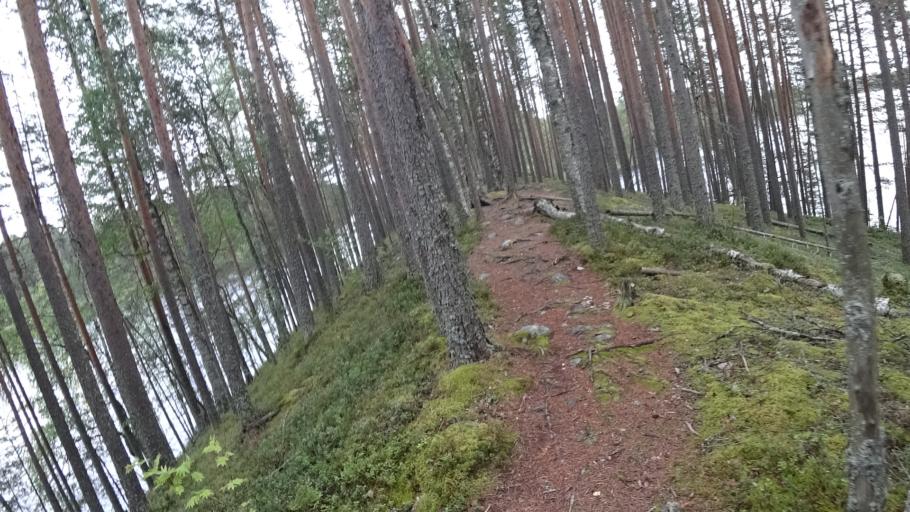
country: FI
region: North Karelia
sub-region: Joensuu
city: Ilomantsi
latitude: 62.5784
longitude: 31.1693
